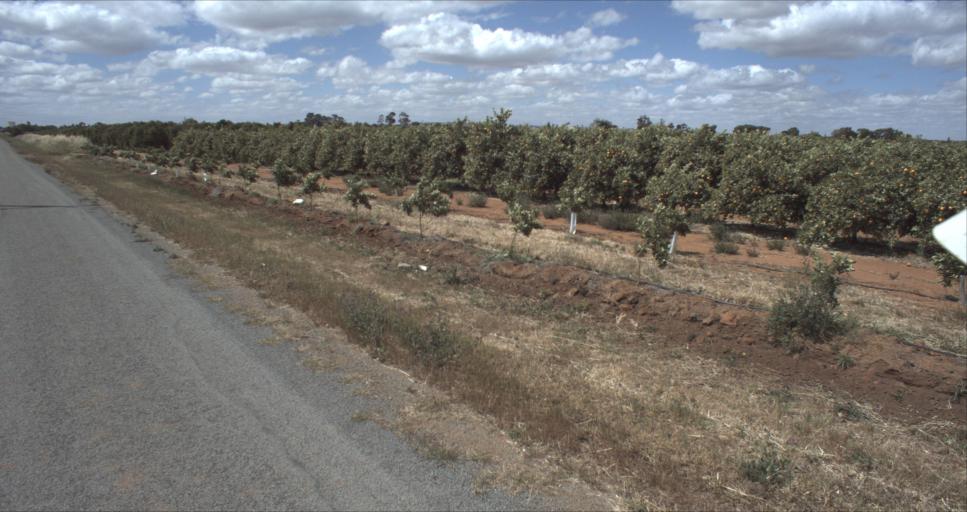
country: AU
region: New South Wales
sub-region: Leeton
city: Leeton
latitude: -34.5830
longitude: 146.3919
